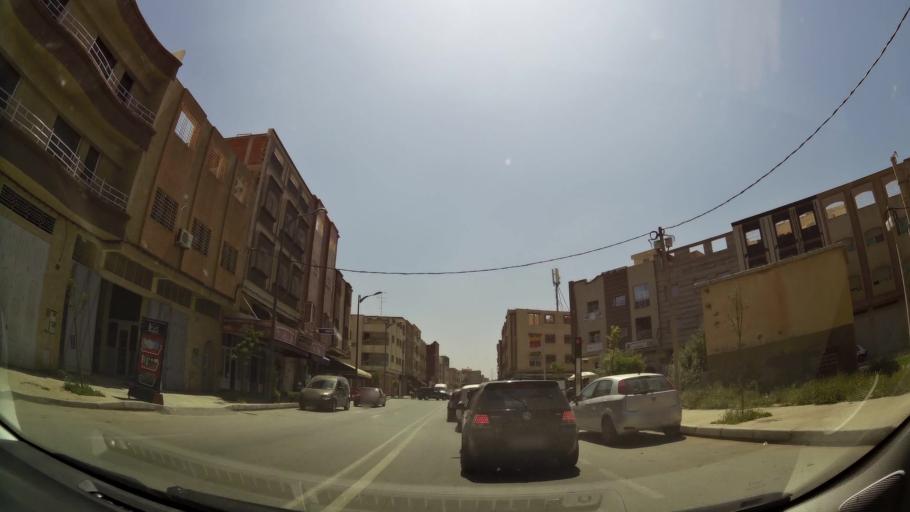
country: MA
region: Oriental
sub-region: Oujda-Angad
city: Oujda
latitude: 34.6918
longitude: -1.8879
